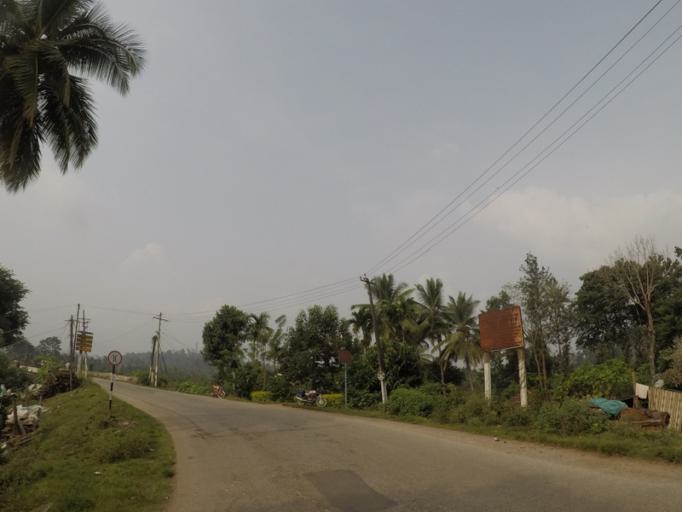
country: IN
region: Karnataka
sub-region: Chikmagalur
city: Koppa
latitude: 13.3530
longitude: 75.4710
